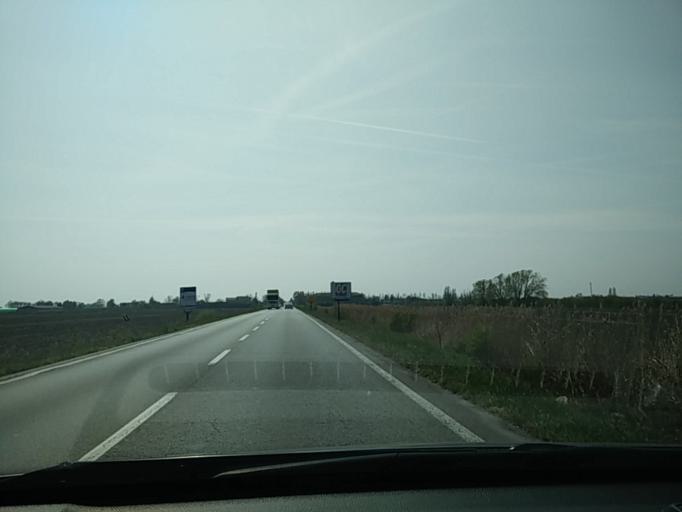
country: IT
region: Veneto
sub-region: Provincia di Venezia
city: Ceggia
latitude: 45.6637
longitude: 12.6151
